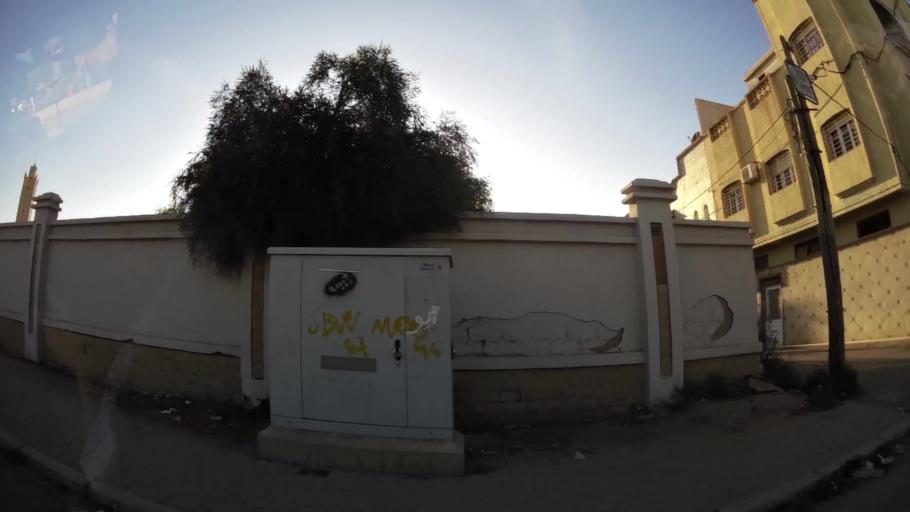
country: MA
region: Oriental
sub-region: Oujda-Angad
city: Oujda
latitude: 34.7009
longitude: -1.8982
